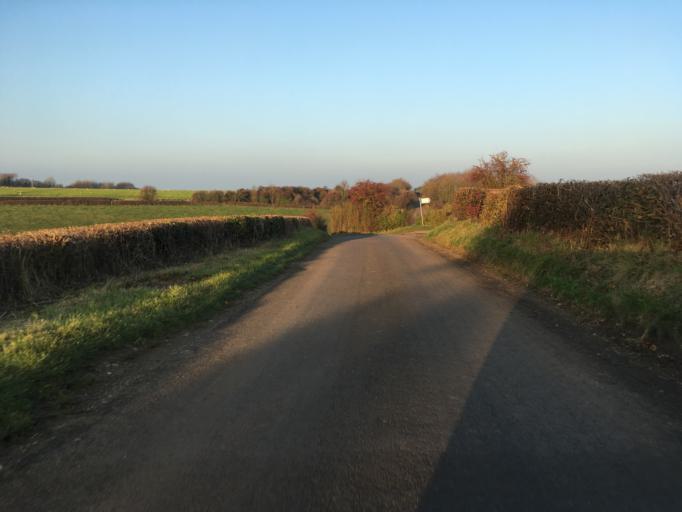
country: GB
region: England
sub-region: Wiltshire
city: Nettleton
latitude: 51.4817
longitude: -2.2651
